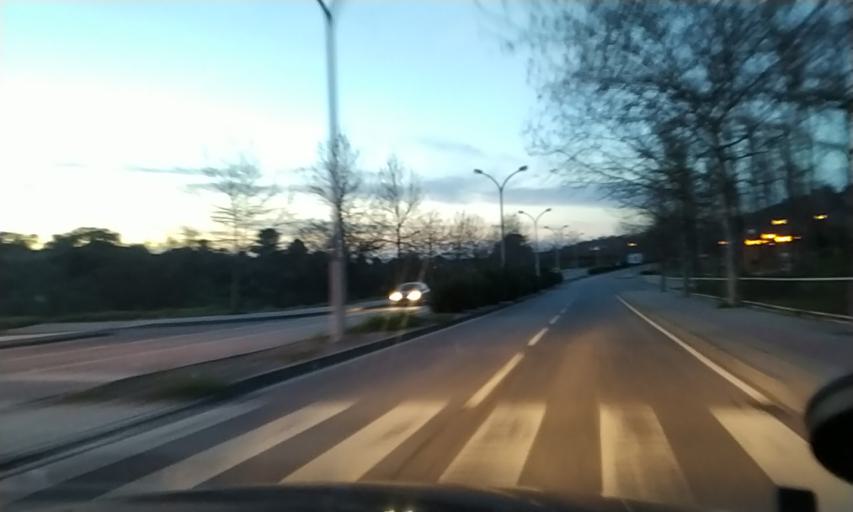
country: PT
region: Castelo Branco
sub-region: Castelo Branco
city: Castelo Branco
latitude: 39.8225
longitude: -7.5086
